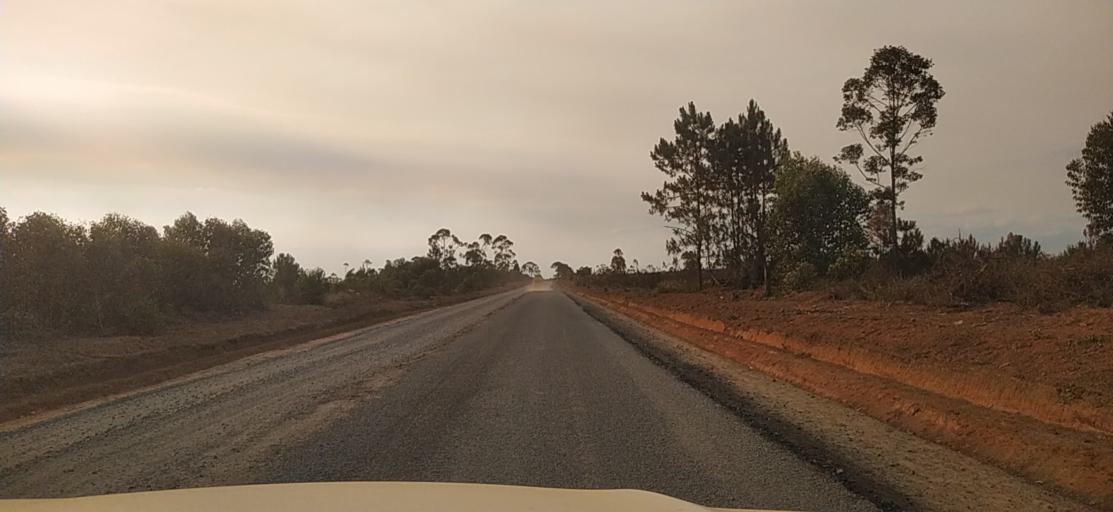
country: MG
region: Alaotra Mangoro
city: Moramanga
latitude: -18.5737
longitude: 48.2683
